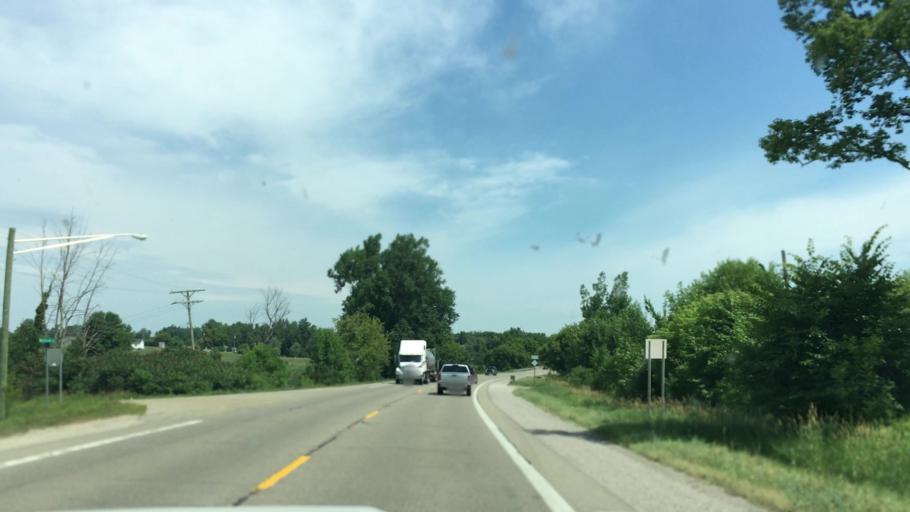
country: US
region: Michigan
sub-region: Lapeer County
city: Imlay City
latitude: 43.0827
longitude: -83.0758
